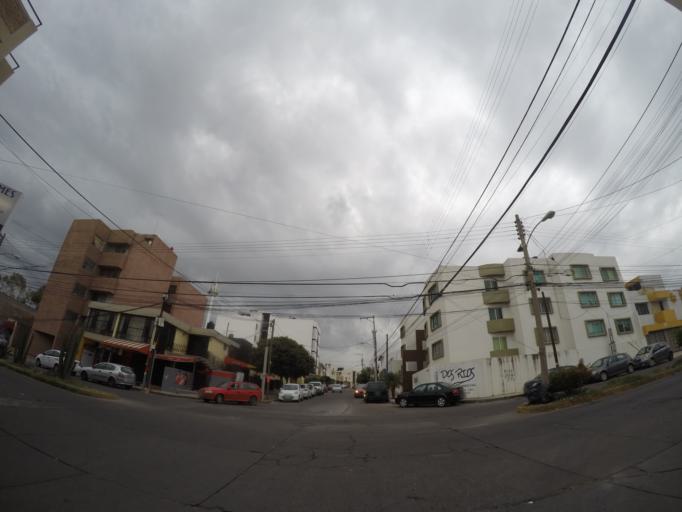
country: MX
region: San Luis Potosi
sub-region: San Luis Potosi
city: San Luis Potosi
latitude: 22.1455
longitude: -101.0174
